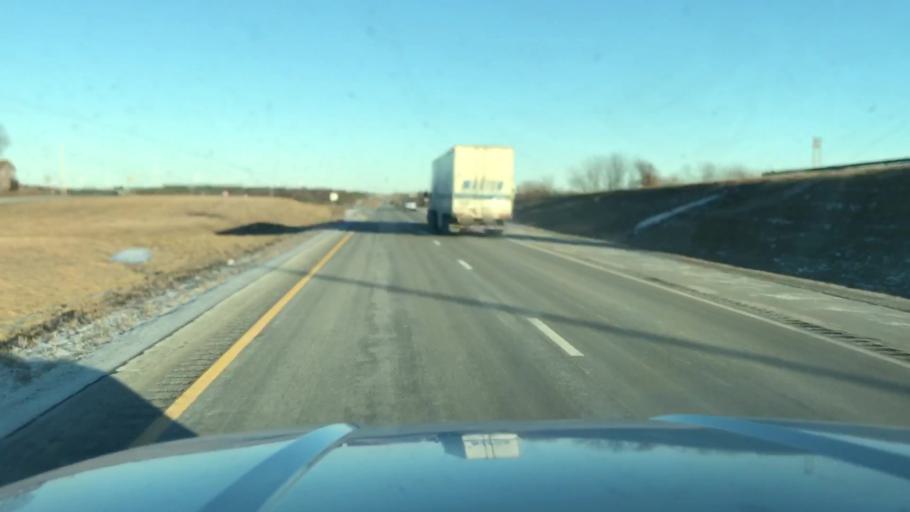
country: US
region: Missouri
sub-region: Clinton County
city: Gower
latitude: 39.7620
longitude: -94.4962
